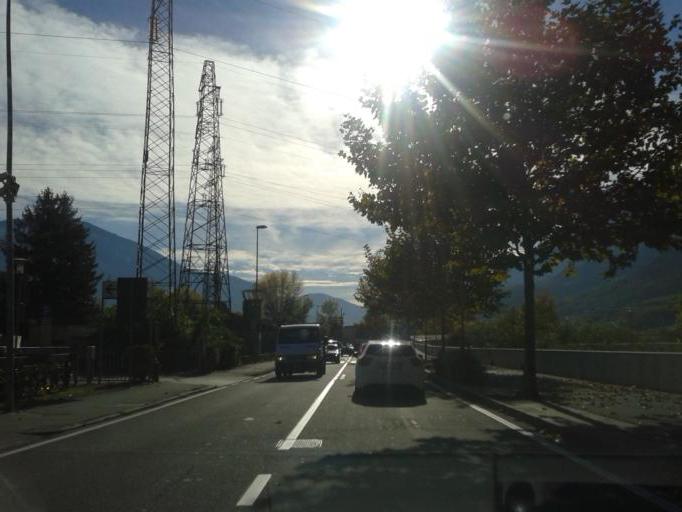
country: IT
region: Trentino-Alto Adige
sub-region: Provincia di Trento
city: Trento
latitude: 46.0576
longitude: 11.1125
